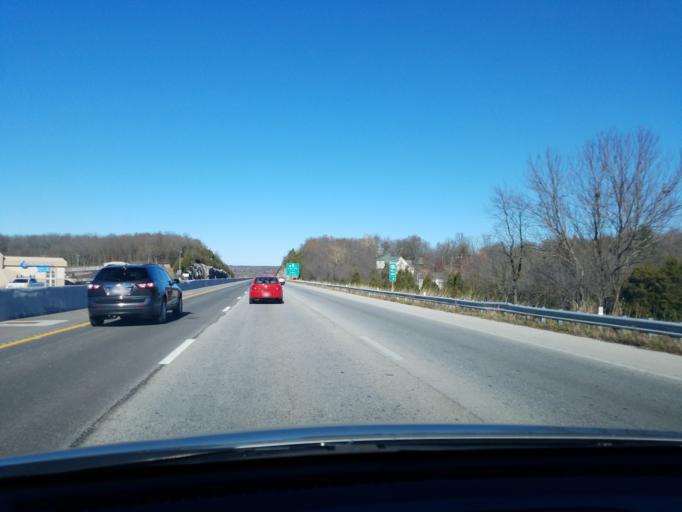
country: US
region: Missouri
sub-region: Christian County
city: Nixa
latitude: 37.1106
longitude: -93.2334
